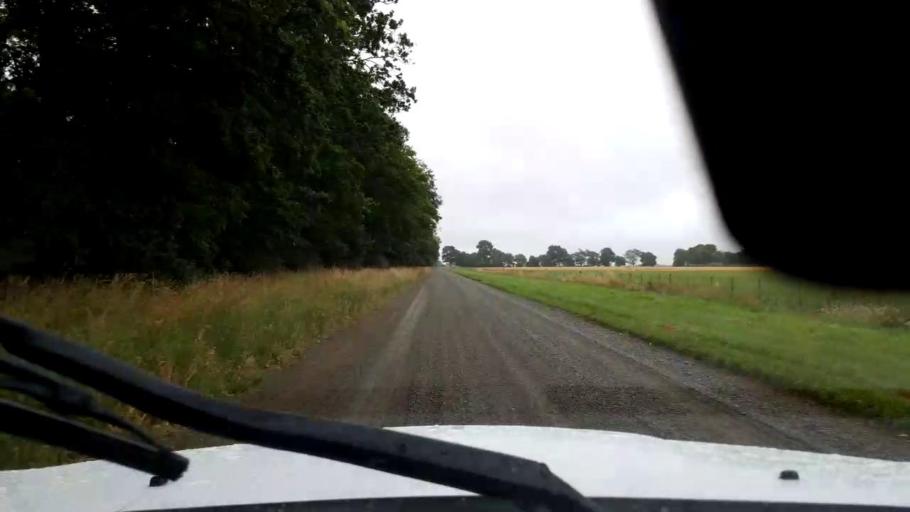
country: NZ
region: Canterbury
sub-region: Timaru District
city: Pleasant Point
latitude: -44.2031
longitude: 171.2814
